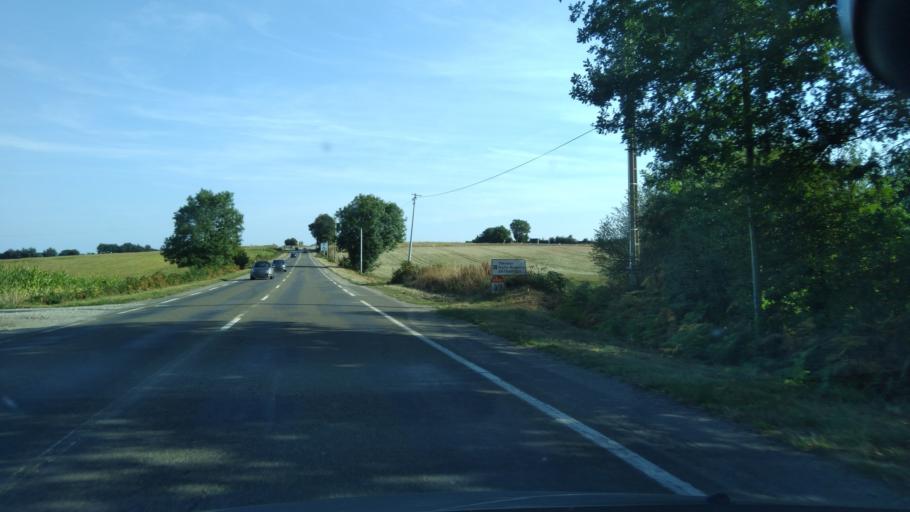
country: FR
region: Pays de la Loire
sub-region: Departement de la Mayenne
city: Entrammes
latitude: 48.0191
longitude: -0.7319
